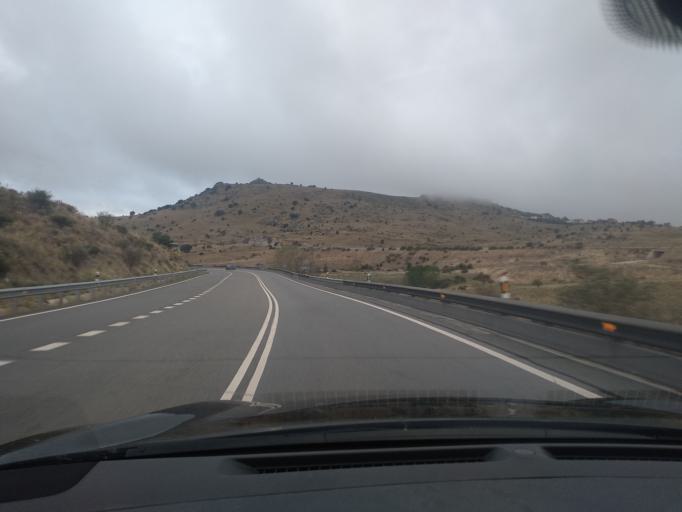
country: ES
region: Castille and Leon
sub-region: Provincia de Segovia
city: Otero de Herreros
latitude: 40.7663
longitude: -4.2054
